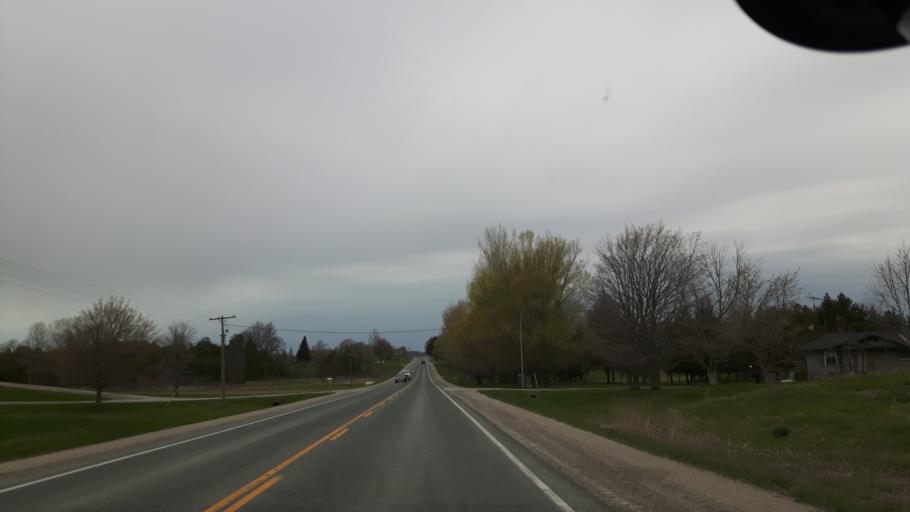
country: CA
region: Ontario
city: Bluewater
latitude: 43.6303
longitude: -81.5702
